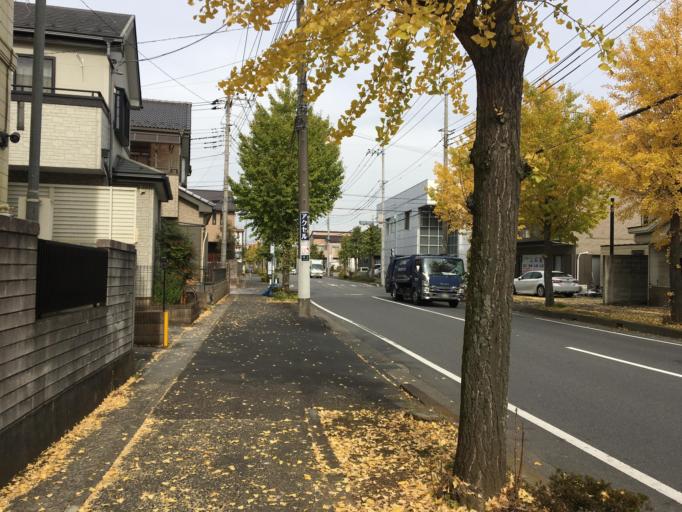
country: JP
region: Saitama
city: Yoshikawa
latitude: 35.8878
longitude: 139.8437
